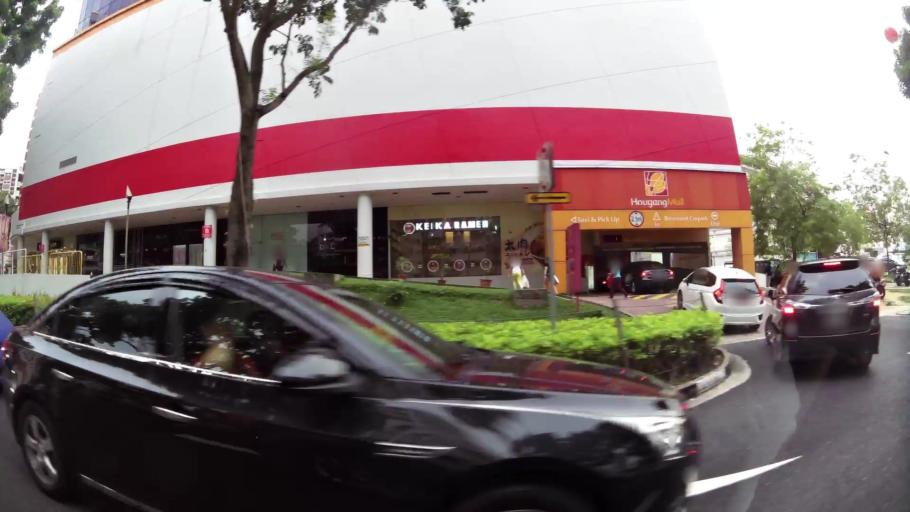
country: SG
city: Singapore
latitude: 1.3729
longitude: 103.8936
